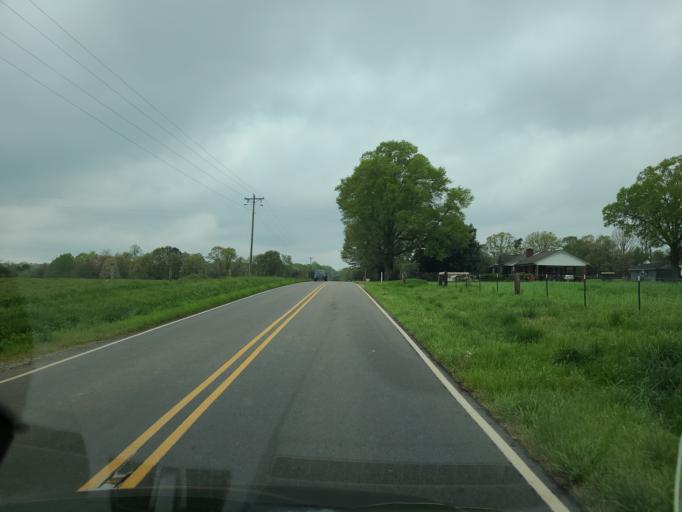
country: US
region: North Carolina
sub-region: Gaston County
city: Cherryville
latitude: 35.4530
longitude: -81.3549
